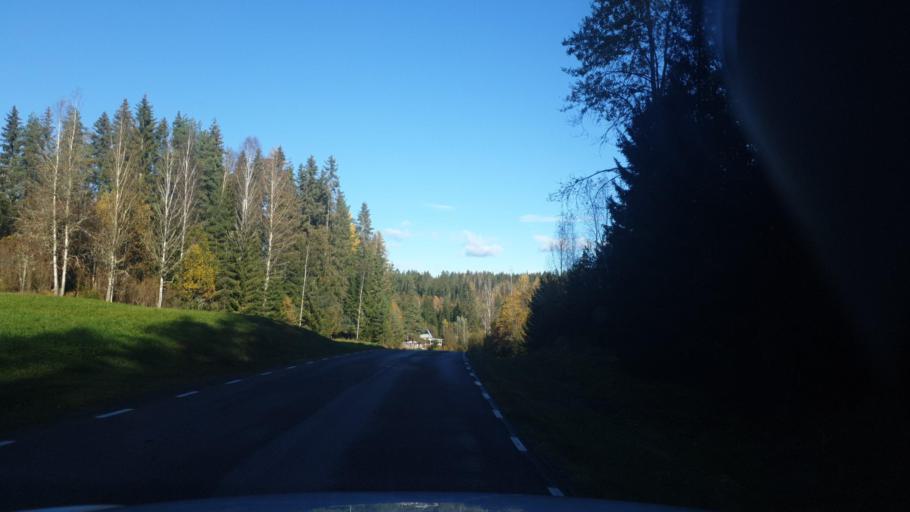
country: SE
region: Vaermland
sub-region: Arvika Kommun
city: Arvika
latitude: 59.6148
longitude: 12.7839
